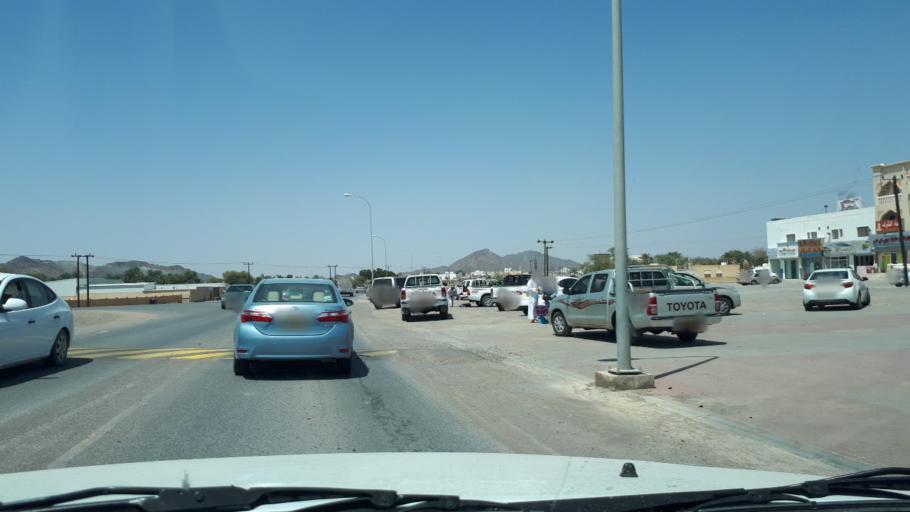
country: OM
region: Muhafazat ad Dakhiliyah
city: Bahla'
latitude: 22.9479
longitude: 57.2833
